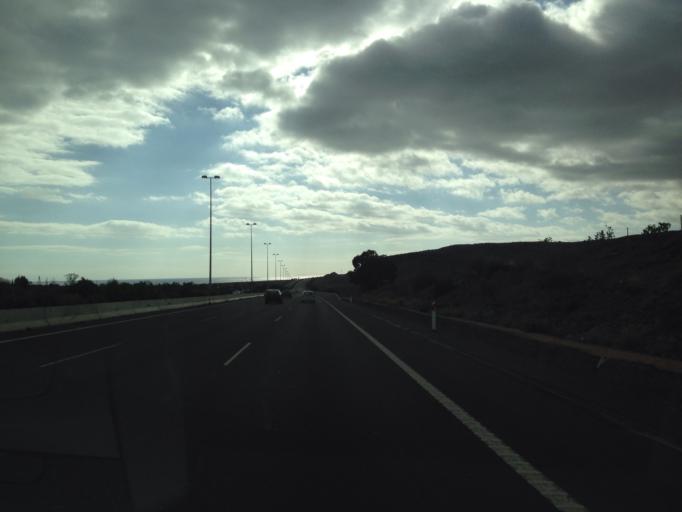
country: ES
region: Canary Islands
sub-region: Provincia de Las Palmas
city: Cruce de Arinaga
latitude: 27.8099
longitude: -15.4783
